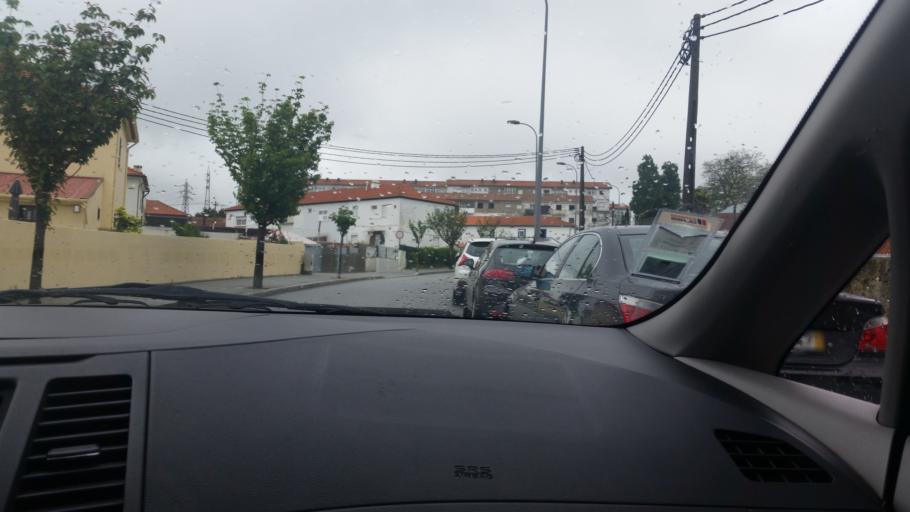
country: PT
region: Porto
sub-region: Matosinhos
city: Matosinhos
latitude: 41.1871
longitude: -8.6808
